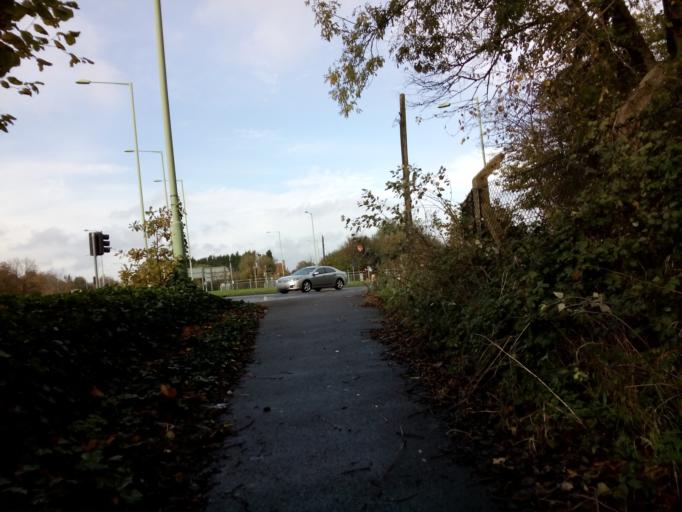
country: GB
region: England
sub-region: Suffolk
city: Stowmarket
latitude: 52.1756
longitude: 1.0115
